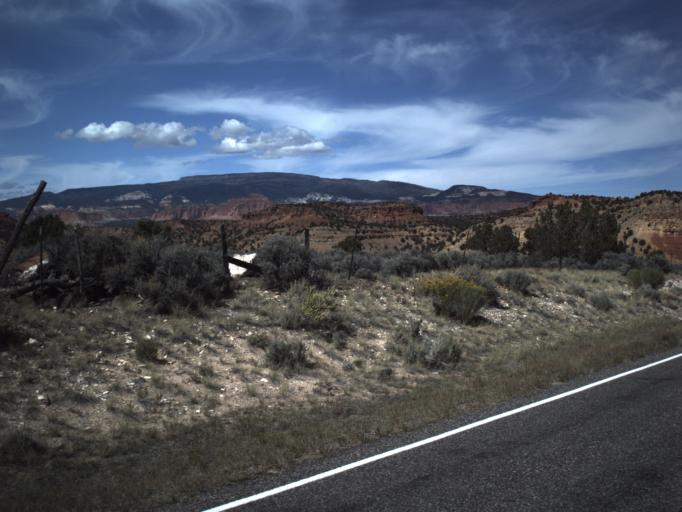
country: US
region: Utah
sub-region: Wayne County
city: Loa
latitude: 38.2653
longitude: -111.3747
